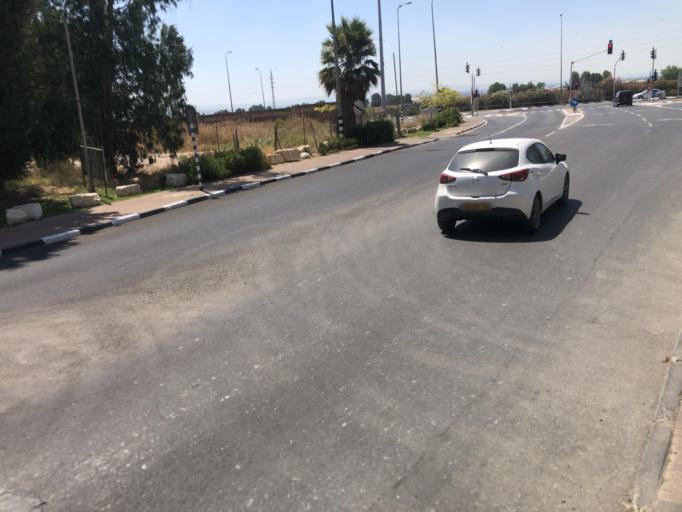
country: IL
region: Tel Aviv
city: Or Yehuda
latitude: 32.0252
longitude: 34.8751
